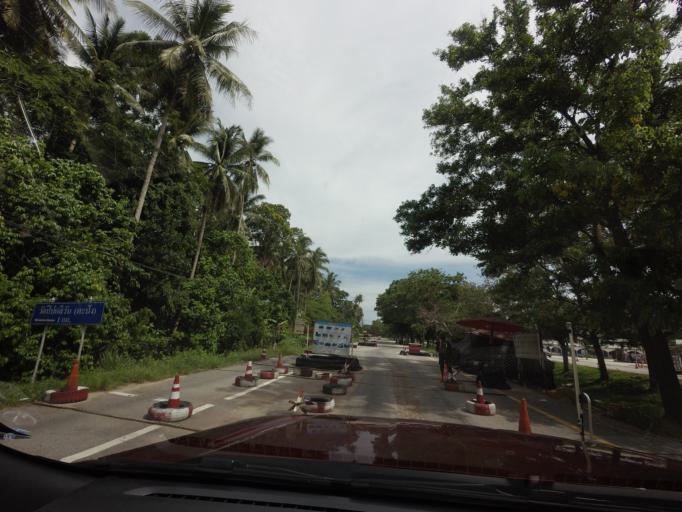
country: TH
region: Narathiwat
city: Tak Bai
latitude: 6.2740
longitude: 102.0229
